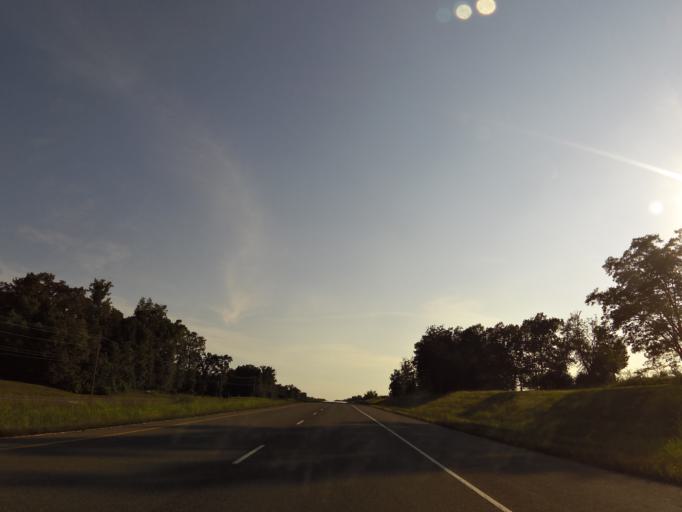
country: US
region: Tennessee
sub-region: McMinn County
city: Englewood
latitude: 35.4519
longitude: -84.4435
